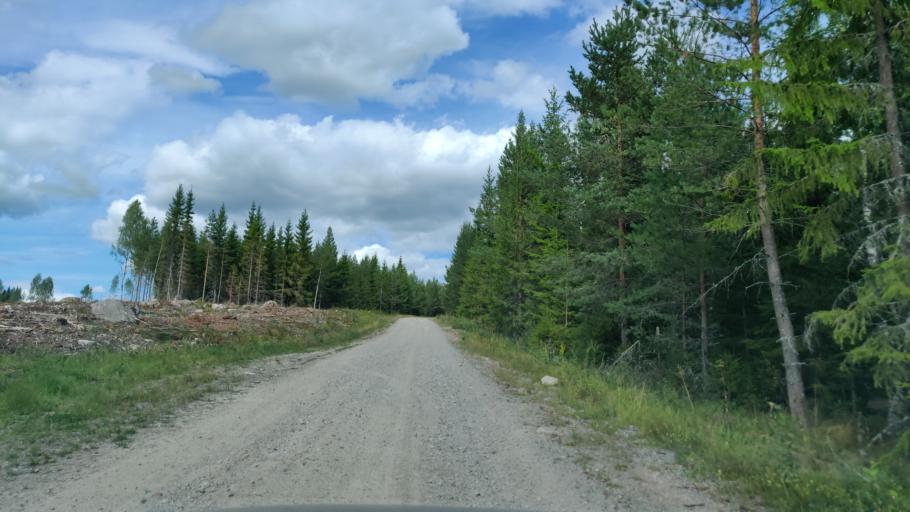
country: SE
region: Vaermland
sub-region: Hagfors Kommun
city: Hagfors
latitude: 60.0101
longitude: 13.7275
